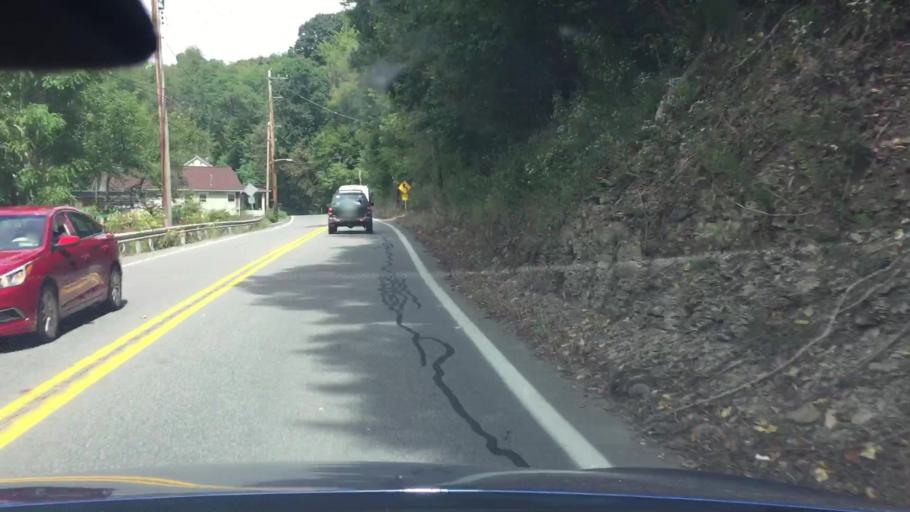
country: US
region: Pennsylvania
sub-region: Allegheny County
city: Cheswick
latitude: 40.5178
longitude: -79.8057
